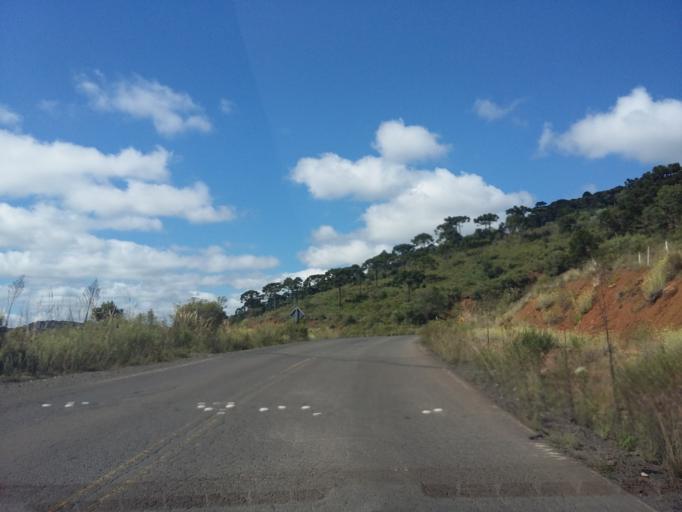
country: BR
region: Santa Catarina
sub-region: Sao Joaquim
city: Sao Joaquim
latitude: -28.0927
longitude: -50.0565
